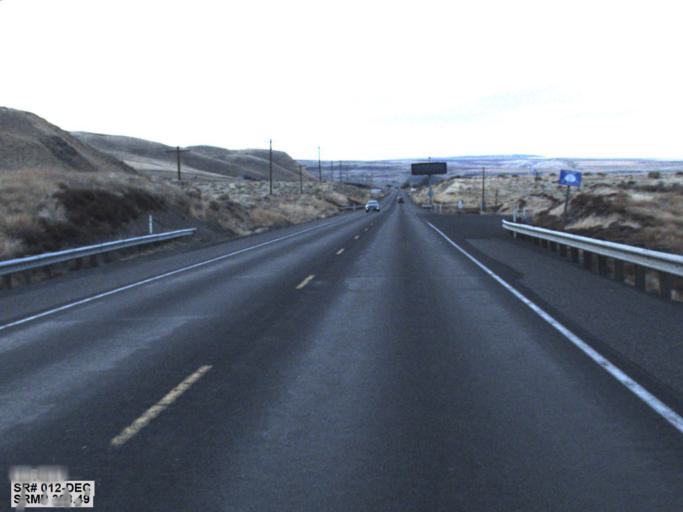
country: US
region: Washington
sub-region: Benton County
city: Finley
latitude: 46.0542
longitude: -118.8905
